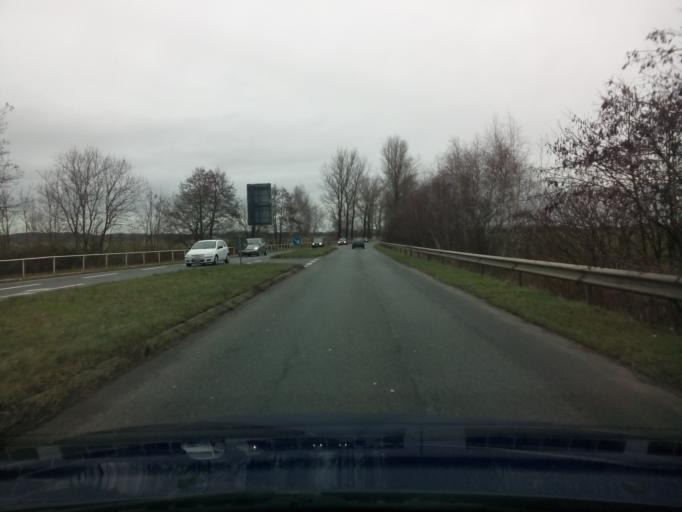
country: DE
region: Lower Saxony
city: Ritterhude
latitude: 53.1469
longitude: 8.7392
